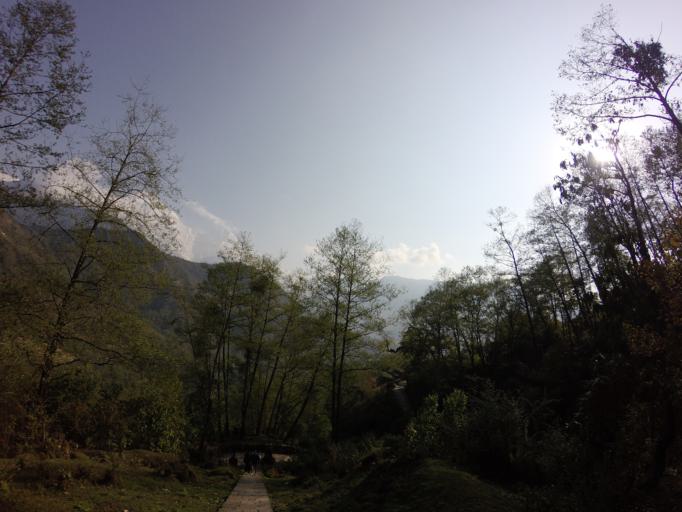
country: NP
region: Western Region
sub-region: Dhawalagiri Zone
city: Chitre
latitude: 28.3813
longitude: 83.8023
